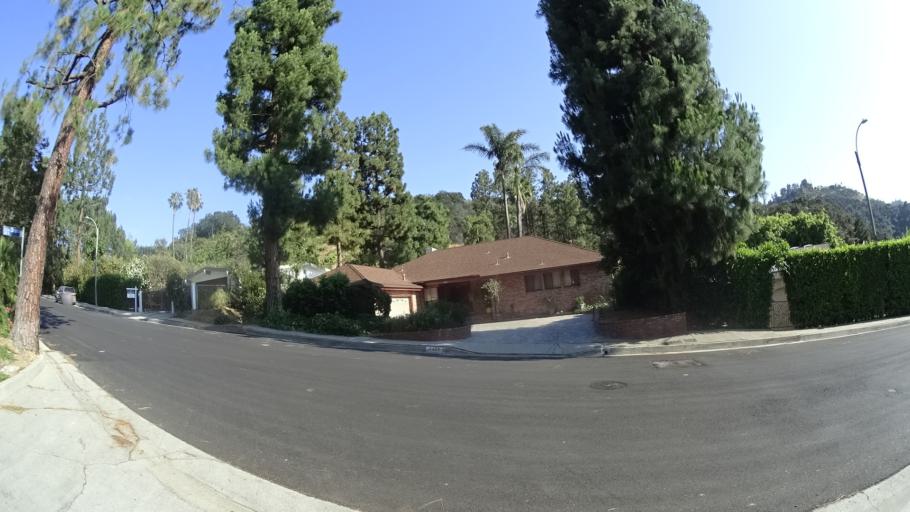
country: US
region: California
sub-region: Los Angeles County
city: Universal City
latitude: 34.1274
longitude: -118.3832
